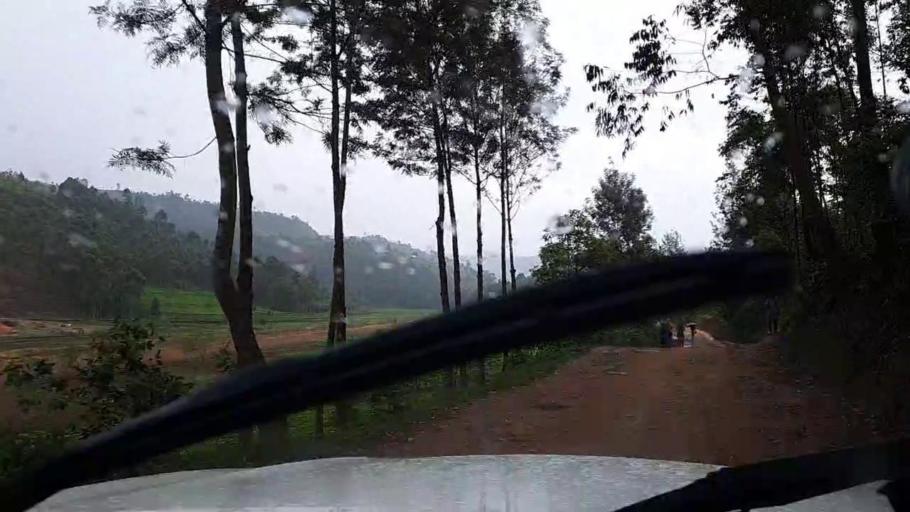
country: RW
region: Northern Province
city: Byumba
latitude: -1.6515
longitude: 29.9312
